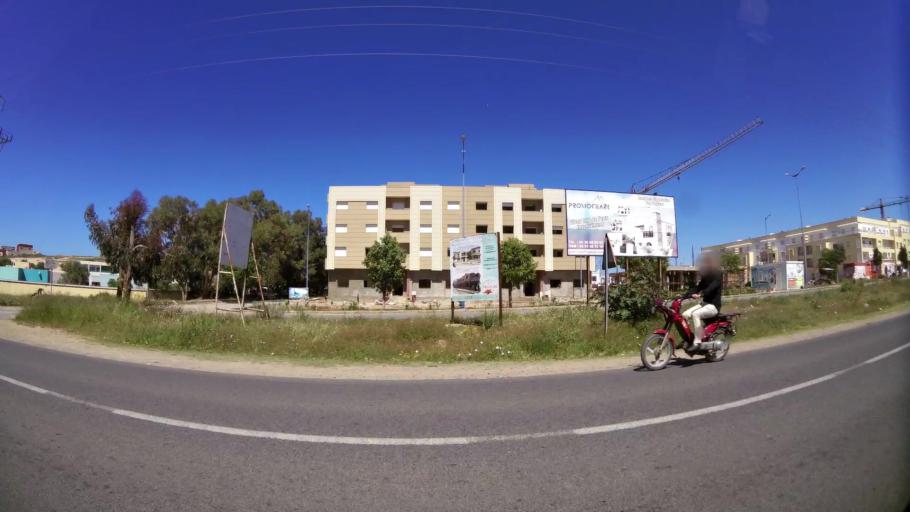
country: MA
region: Oriental
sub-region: Berkane-Taourirt
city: Madagh
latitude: 35.1249
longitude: -2.4226
